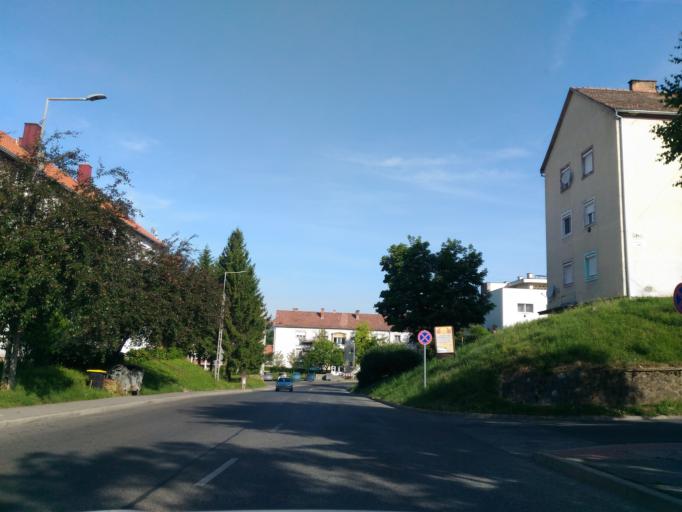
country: HU
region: Baranya
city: Komlo
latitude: 46.1845
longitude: 18.2576
